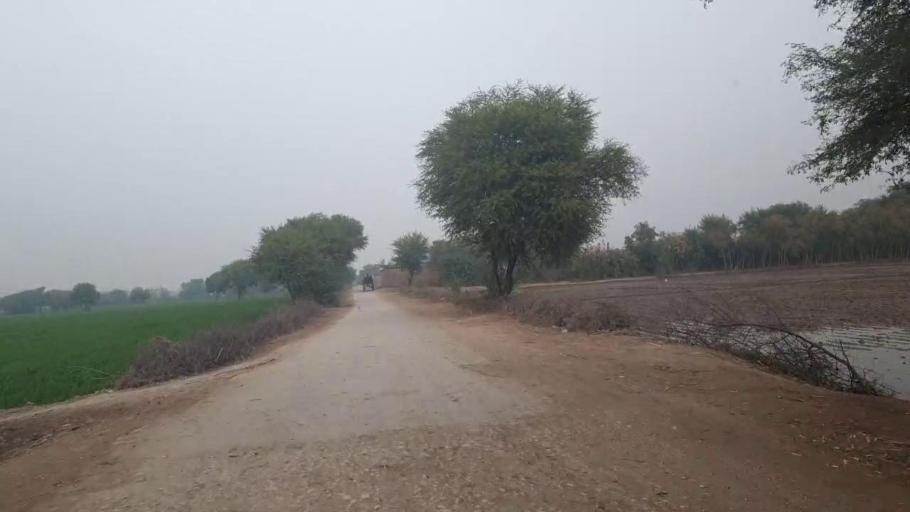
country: PK
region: Sindh
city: Tando Adam
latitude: 25.7778
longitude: 68.6985
